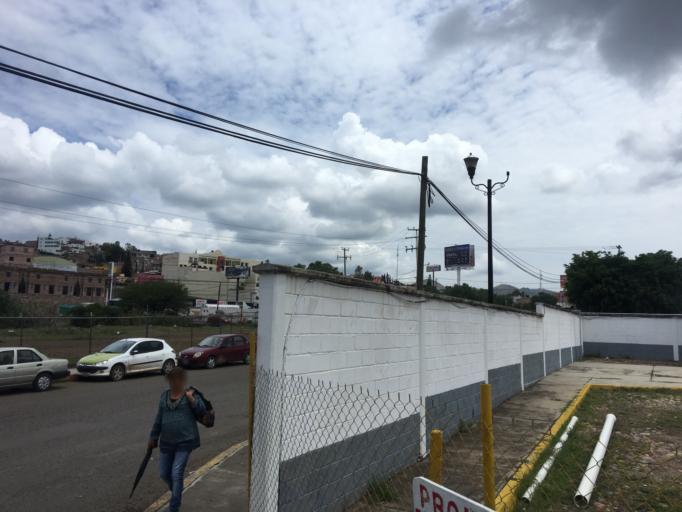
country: MX
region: Guanajuato
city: Marfil
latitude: 20.9830
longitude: -101.2877
